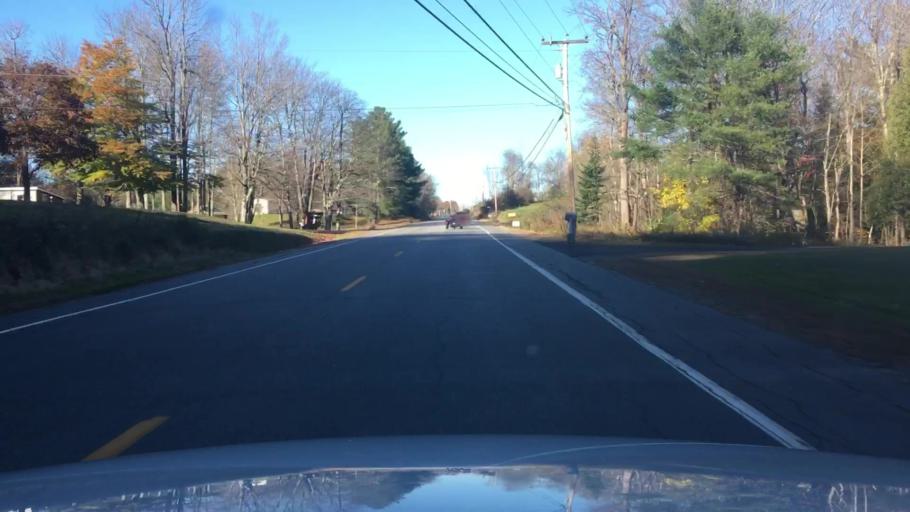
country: US
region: Maine
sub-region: Sagadahoc County
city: Topsham
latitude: 44.0401
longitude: -69.9422
